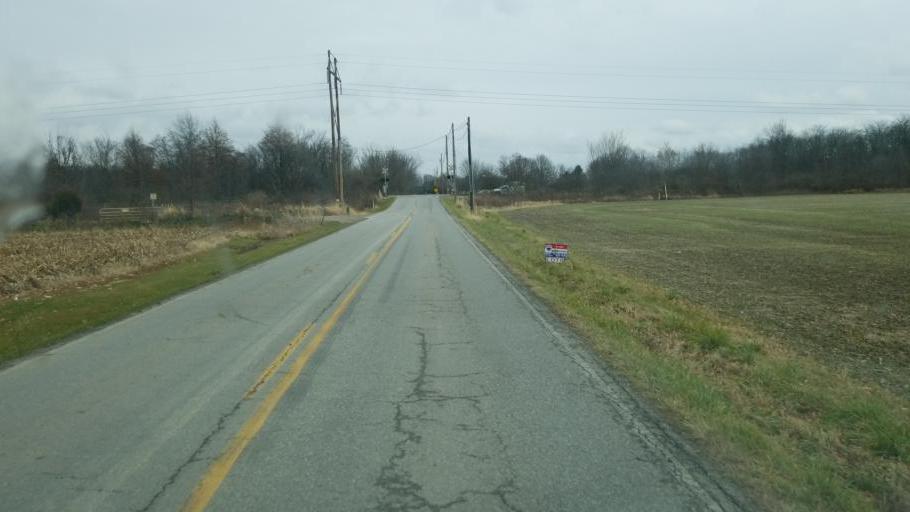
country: US
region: Ohio
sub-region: Delaware County
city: Delaware
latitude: 40.2534
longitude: -83.0868
